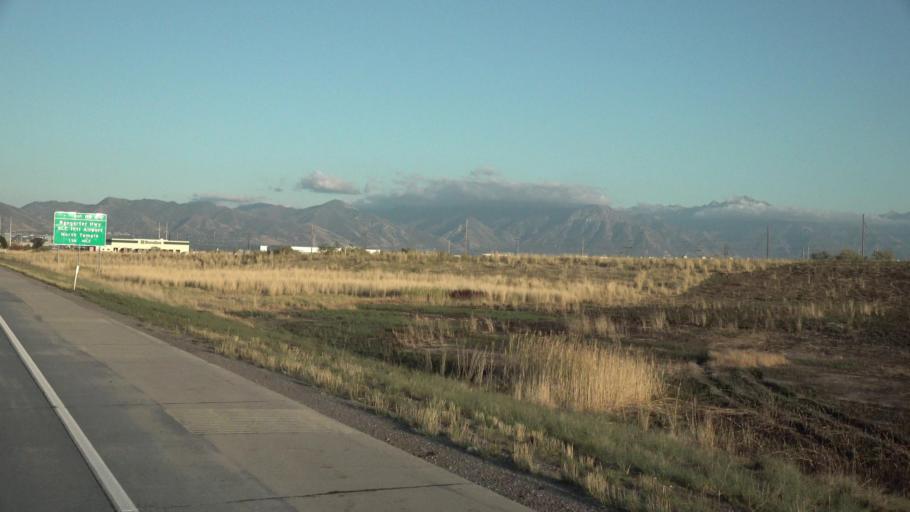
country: US
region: Utah
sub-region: Salt Lake County
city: West Valley City
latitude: 40.7709
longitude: -112.0222
